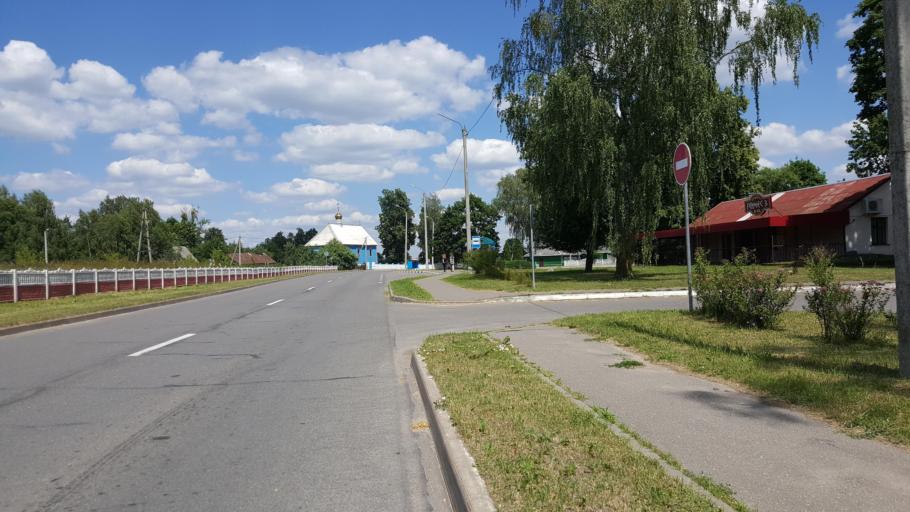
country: BY
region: Brest
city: Kamyanyuki
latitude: 52.4898
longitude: 23.7782
